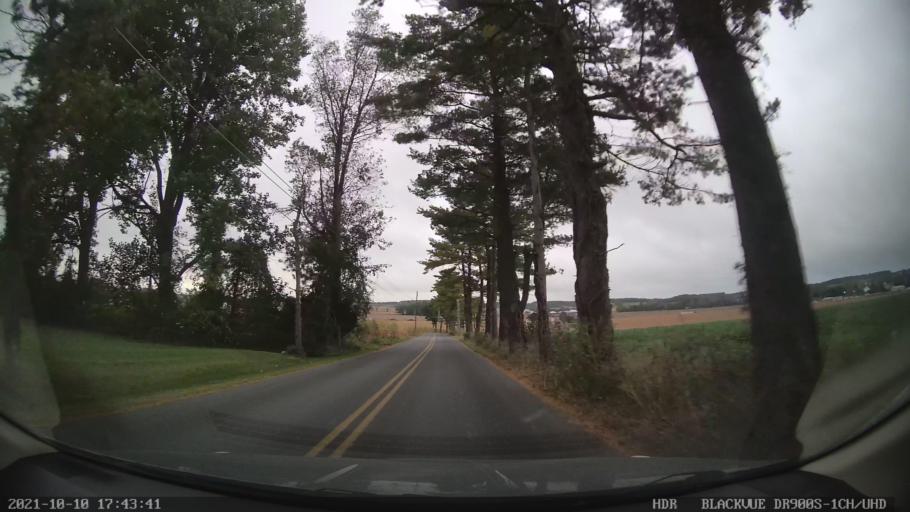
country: US
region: Pennsylvania
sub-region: Berks County
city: Topton
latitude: 40.5394
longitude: -75.6773
